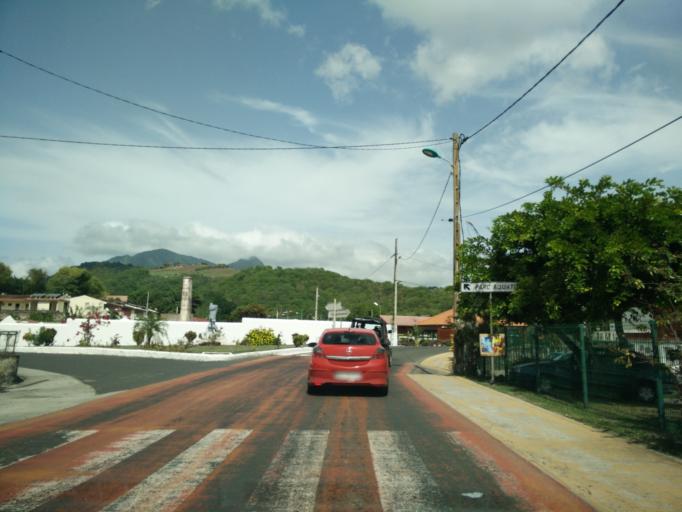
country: MQ
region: Martinique
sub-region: Martinique
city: Saint-Pierre
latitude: 14.7111
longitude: -61.1836
